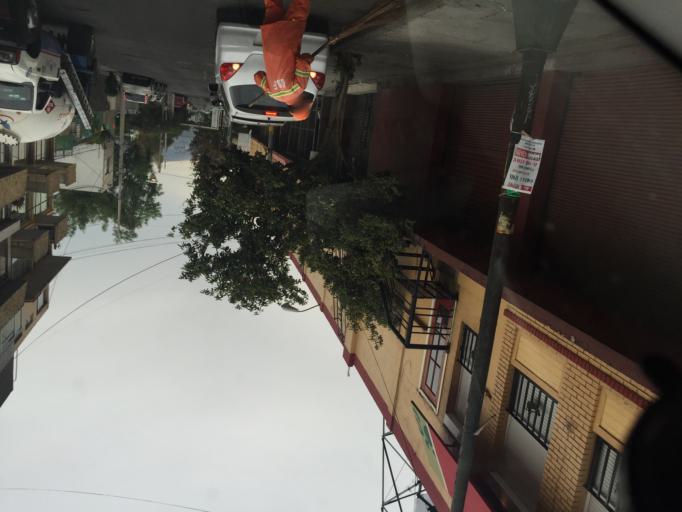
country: MX
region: Mexico
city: Colonia Lindavista
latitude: 19.4936
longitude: -99.1328
